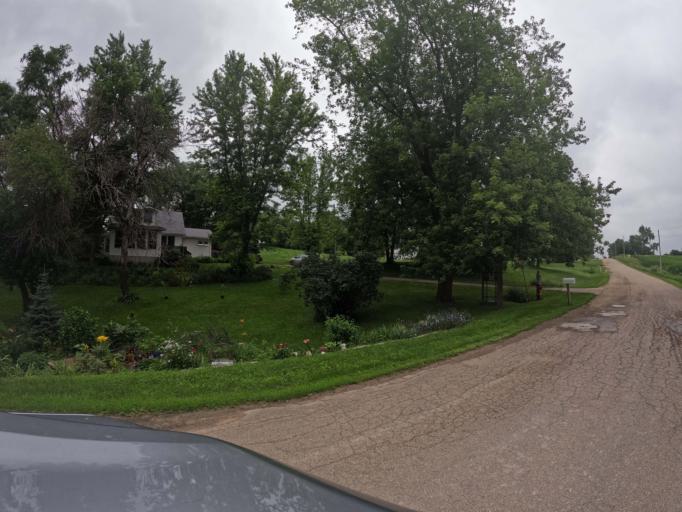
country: US
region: Iowa
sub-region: Clinton County
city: De Witt
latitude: 41.9129
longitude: -90.6065
